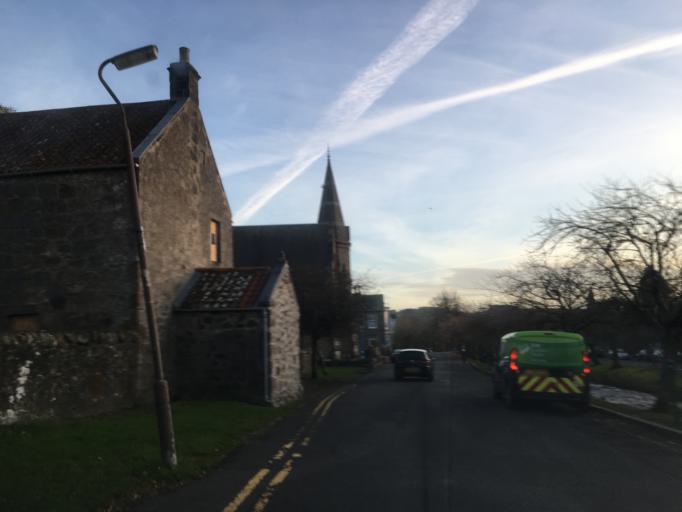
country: GB
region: Scotland
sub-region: Clackmannanshire
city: Dollar
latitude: 56.1643
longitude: -3.6712
